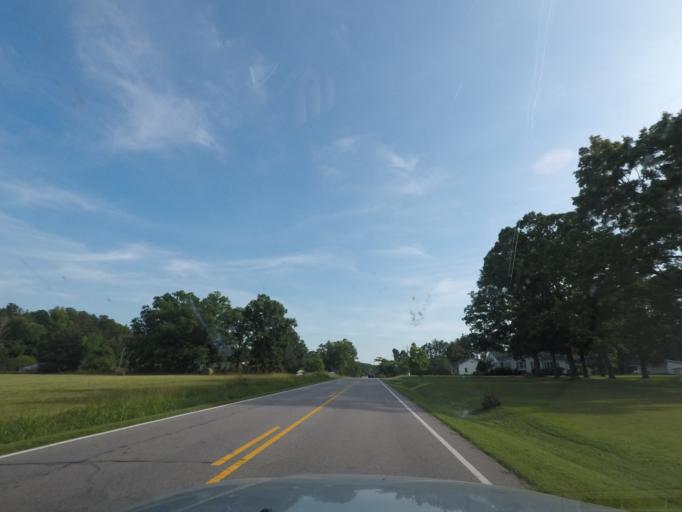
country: US
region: Virginia
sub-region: Mecklenburg County
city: Clarksville
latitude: 36.4955
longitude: -78.5432
